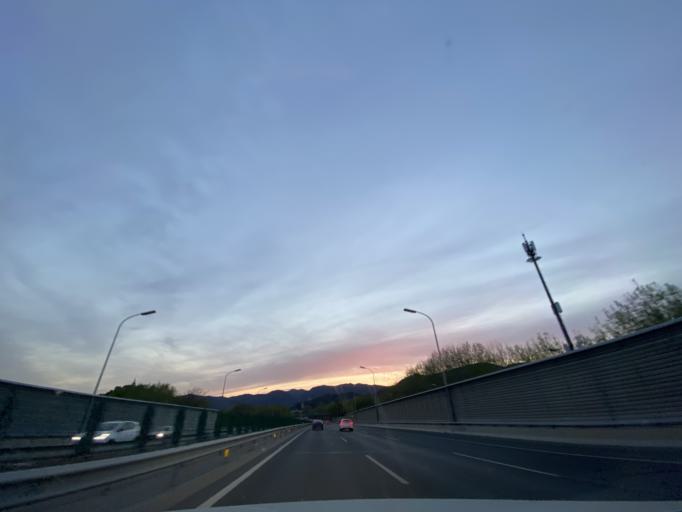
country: CN
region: Beijing
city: Haidian
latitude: 40.0016
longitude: 116.2493
